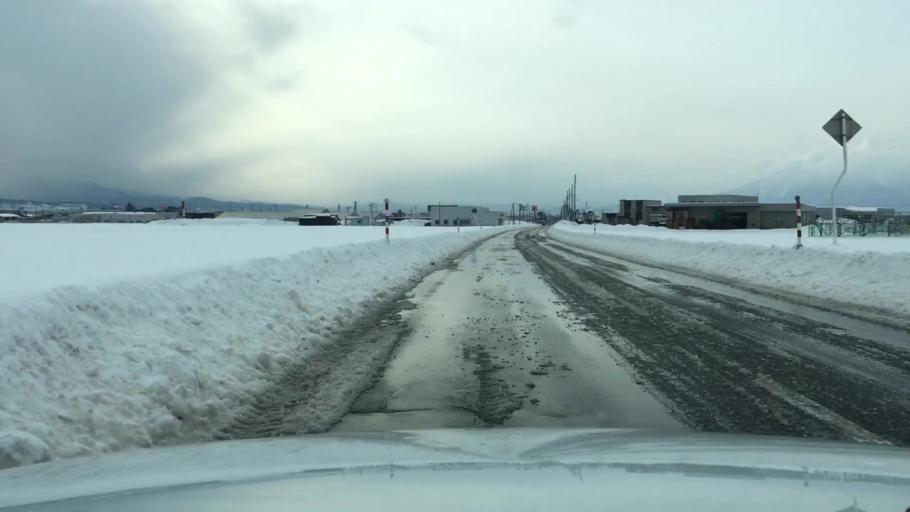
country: JP
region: Aomori
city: Kuroishi
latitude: 40.5916
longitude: 140.5753
